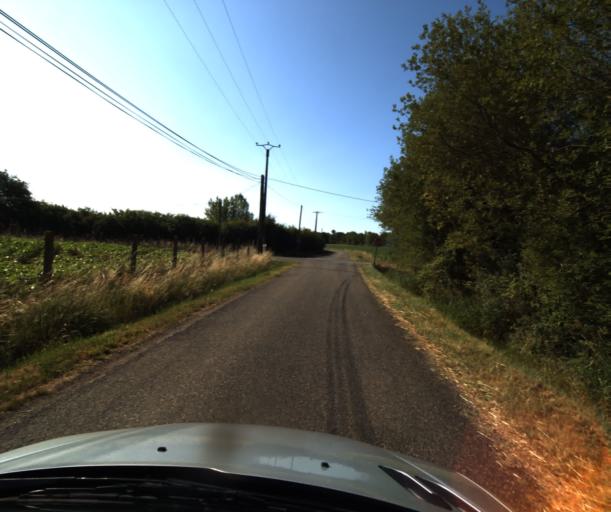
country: FR
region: Midi-Pyrenees
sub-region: Departement du Tarn-et-Garonne
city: Bressols
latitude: 43.9582
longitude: 1.2865
